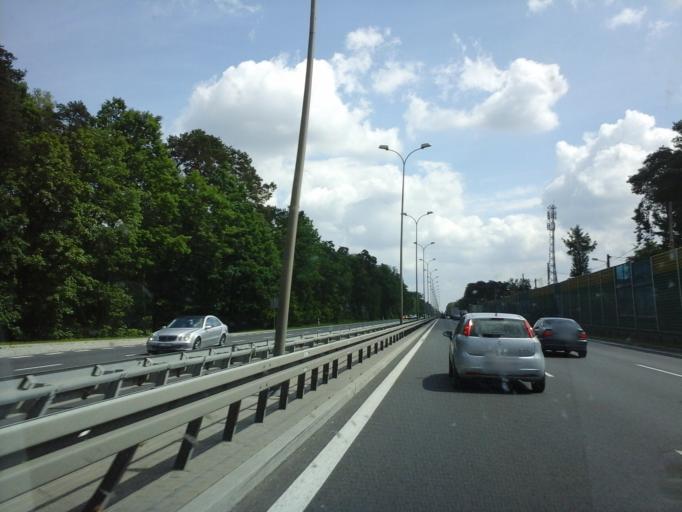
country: PL
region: Lodz Voivodeship
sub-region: Powiat lodzki wschodni
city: Tuszyn
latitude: 51.6218
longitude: 19.5170
